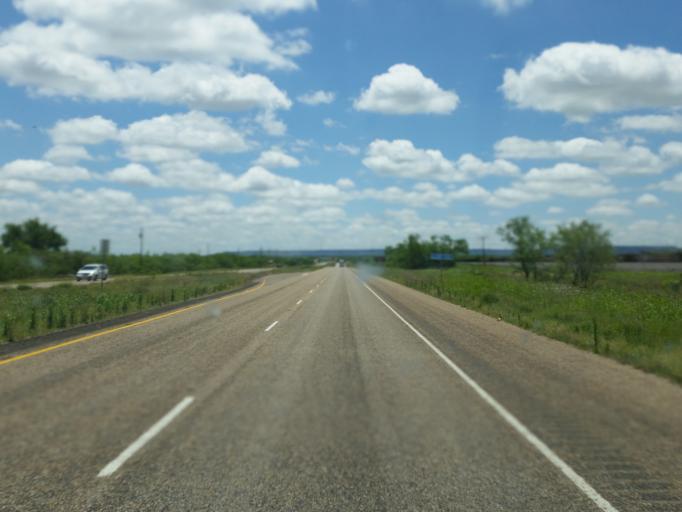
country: US
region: Texas
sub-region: Garza County
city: Post
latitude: 33.0510
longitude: -101.2097
